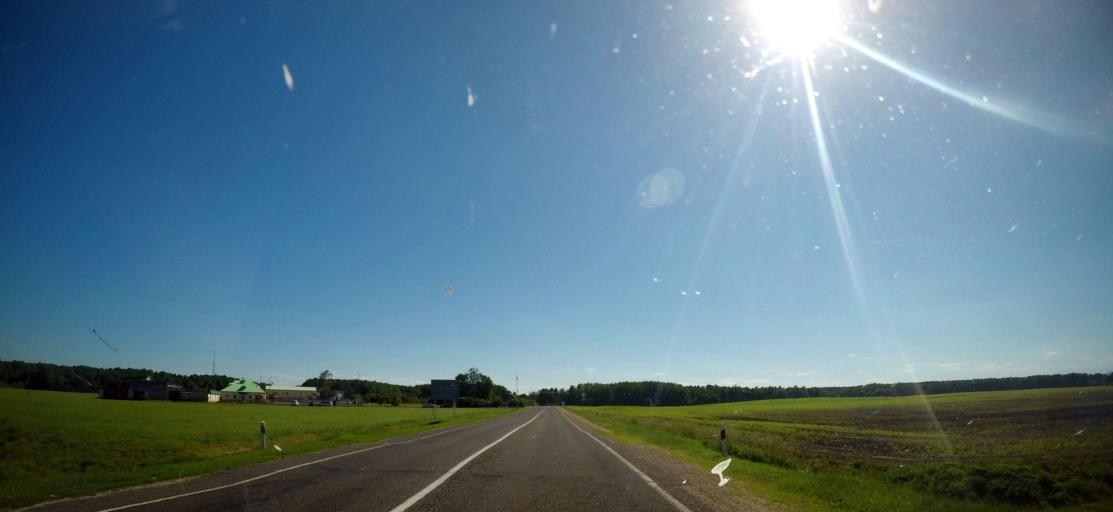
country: BY
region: Grodnenskaya
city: Vyalikaya Byerastavitsa
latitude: 53.1799
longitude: 24.0039
